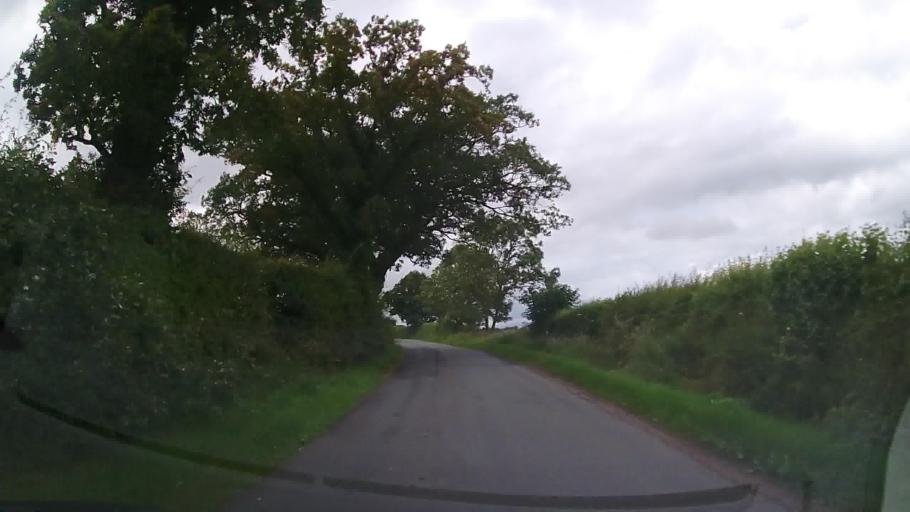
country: GB
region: England
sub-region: Shropshire
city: Wem
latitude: 52.9079
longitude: -2.7293
